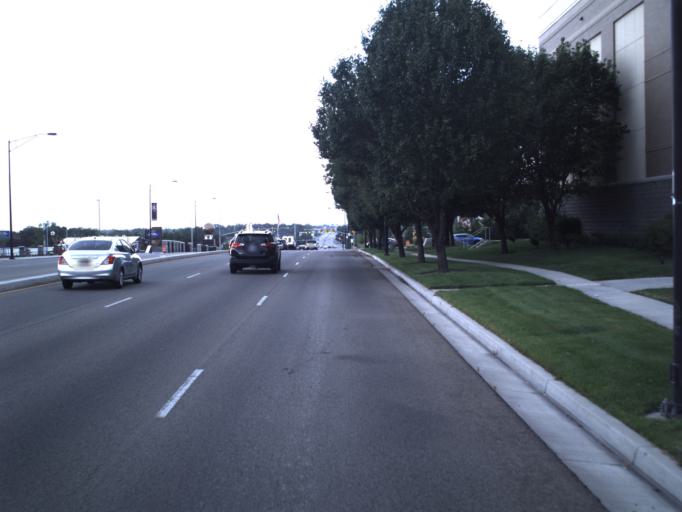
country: US
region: Utah
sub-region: Salt Lake County
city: Sandy City
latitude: 40.5819
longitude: -111.8907
